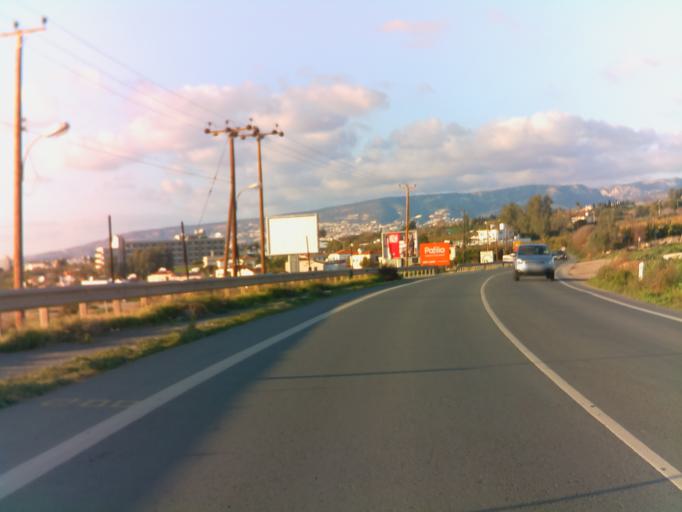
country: CY
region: Pafos
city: Kissonerga
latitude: 34.8159
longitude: 32.3951
